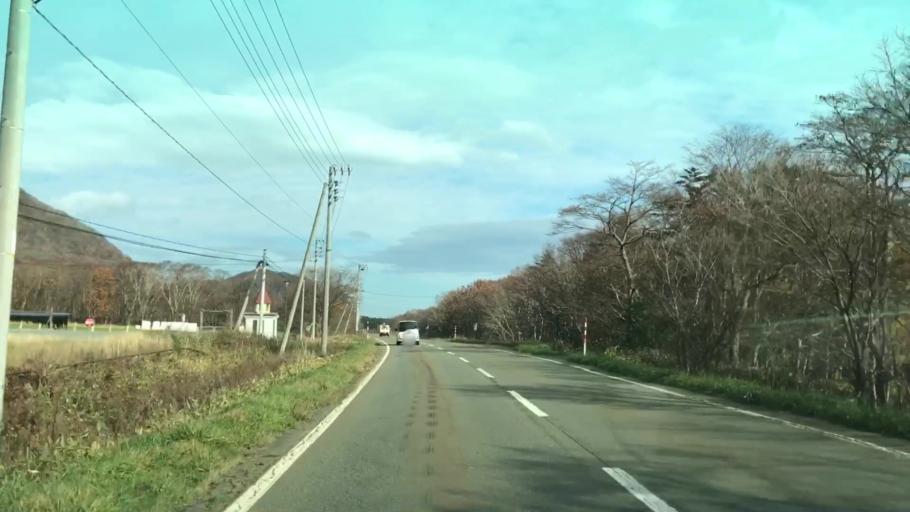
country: JP
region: Hokkaido
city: Obihiro
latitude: 42.0242
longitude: 143.2649
